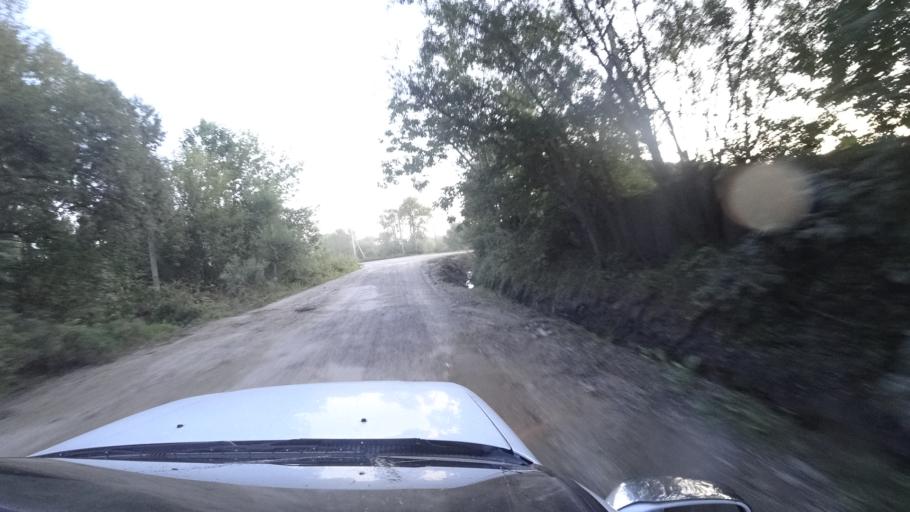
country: RU
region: Primorskiy
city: Dal'nerechensk
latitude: 45.9348
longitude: 133.7585
